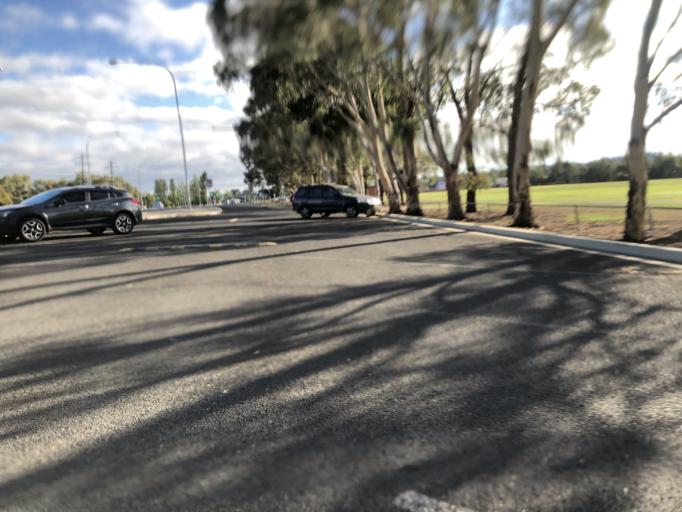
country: AU
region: New South Wales
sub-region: Orange Municipality
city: Orange
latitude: -33.3081
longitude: 149.0977
